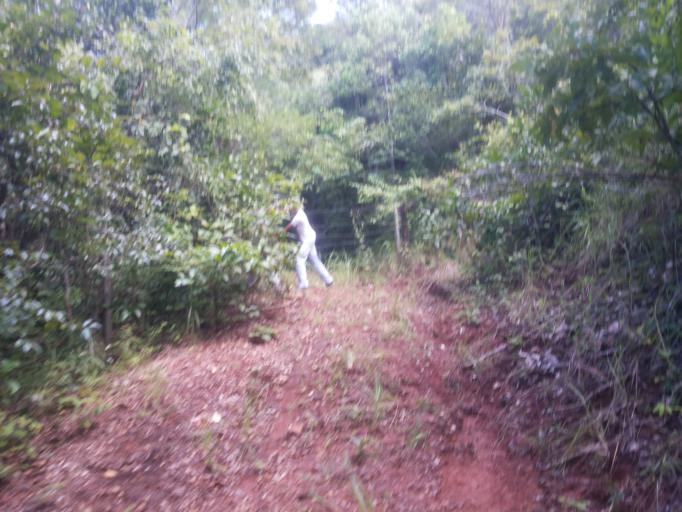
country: BR
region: Minas Gerais
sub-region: Ituiutaba
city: Ituiutaba
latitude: -19.0348
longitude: -49.4669
